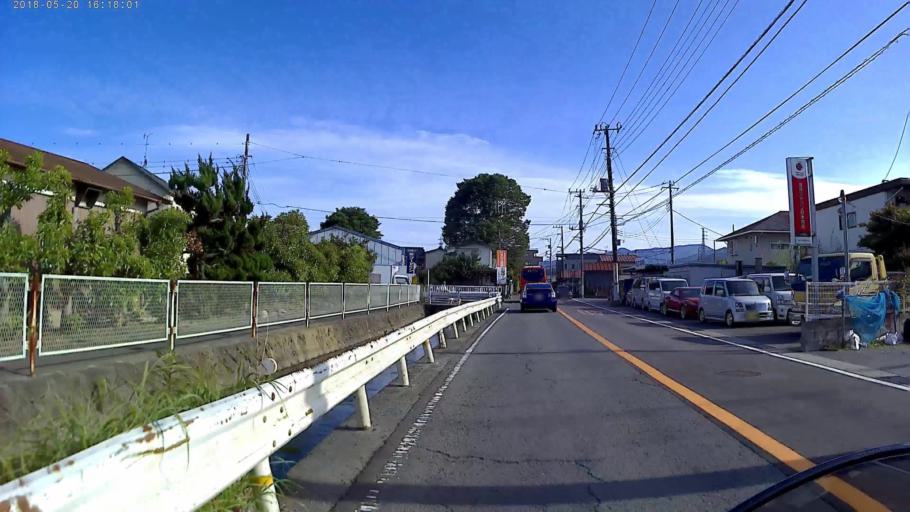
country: JP
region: Kanagawa
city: Odawara
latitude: 35.3043
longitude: 139.1454
